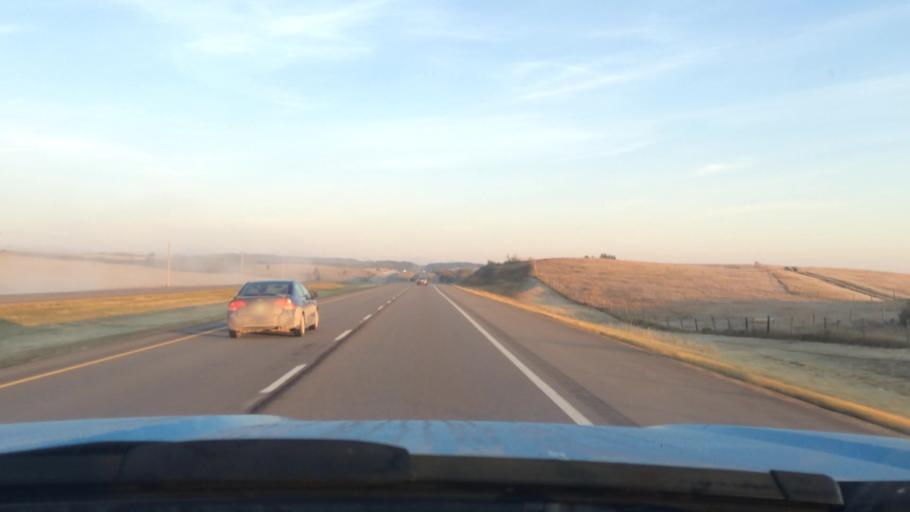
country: CA
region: Alberta
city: Cochrane
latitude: 51.1146
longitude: -114.6523
